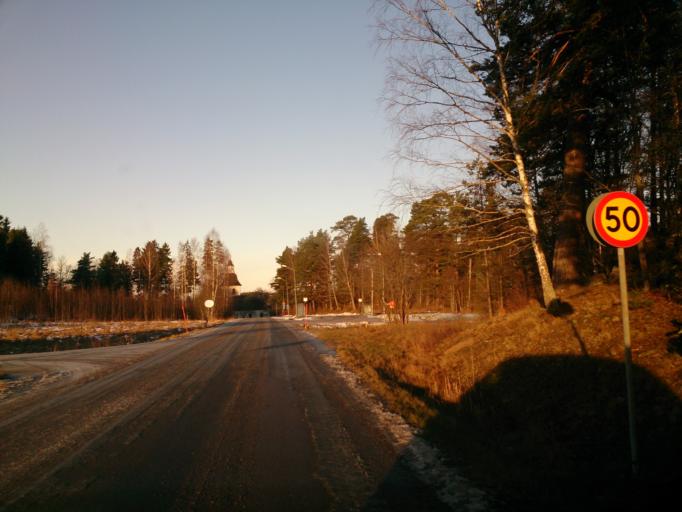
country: SE
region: OEstergoetland
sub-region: Linkopings Kommun
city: Sturefors
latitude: 58.2966
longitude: 15.8689
